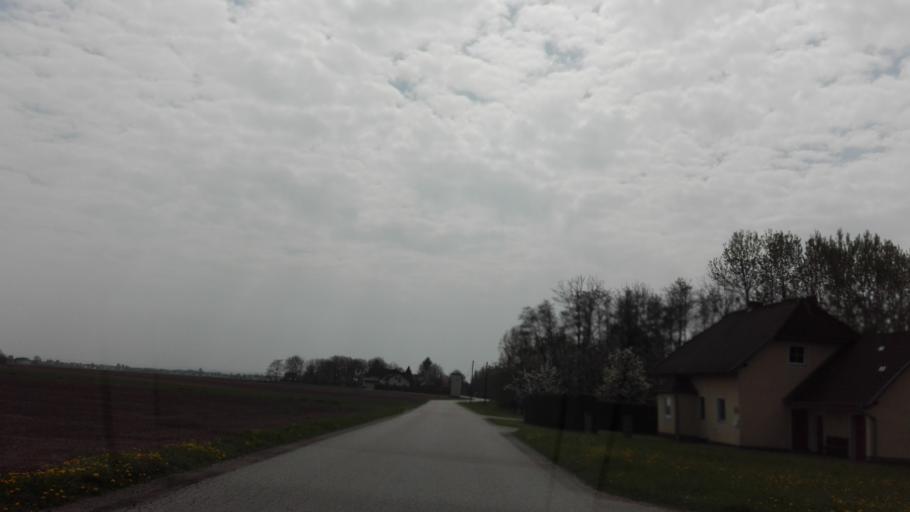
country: AT
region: Upper Austria
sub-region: Politischer Bezirk Perg
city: Perg
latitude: 48.2427
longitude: 14.5976
